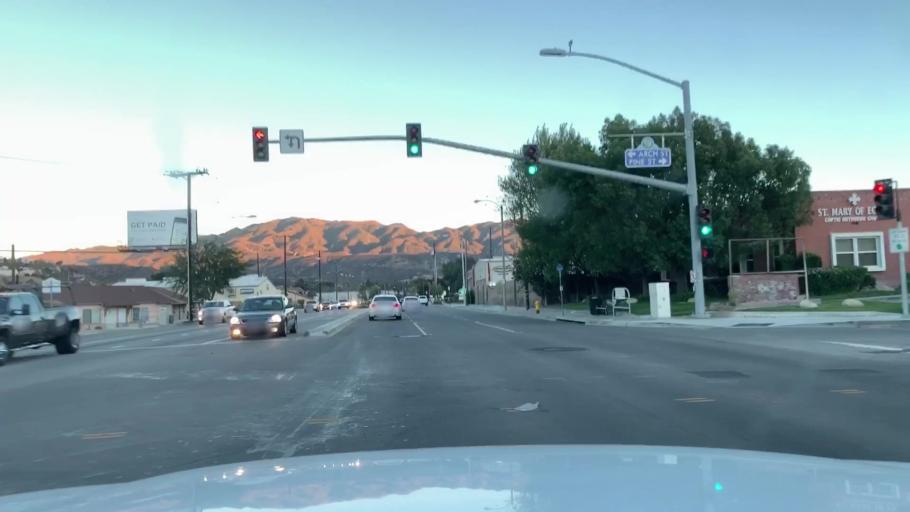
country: US
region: California
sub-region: Los Angeles County
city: Santa Clarita
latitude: 34.3746
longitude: -118.5222
